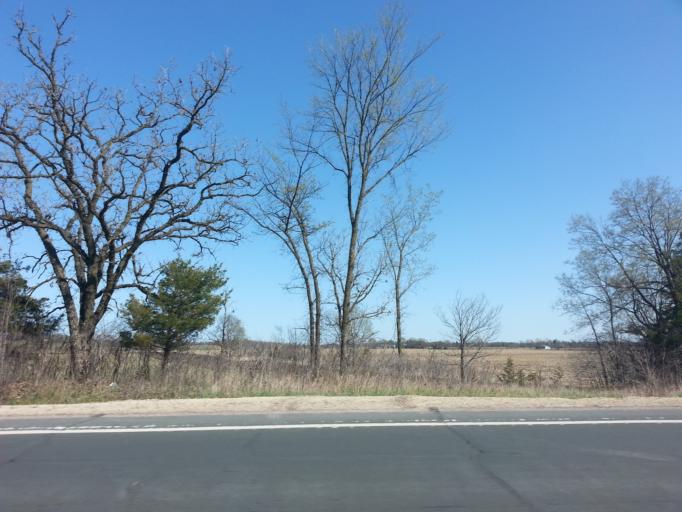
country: US
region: Wisconsin
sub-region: Pepin County
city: Durand
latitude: 44.7168
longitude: -91.9336
